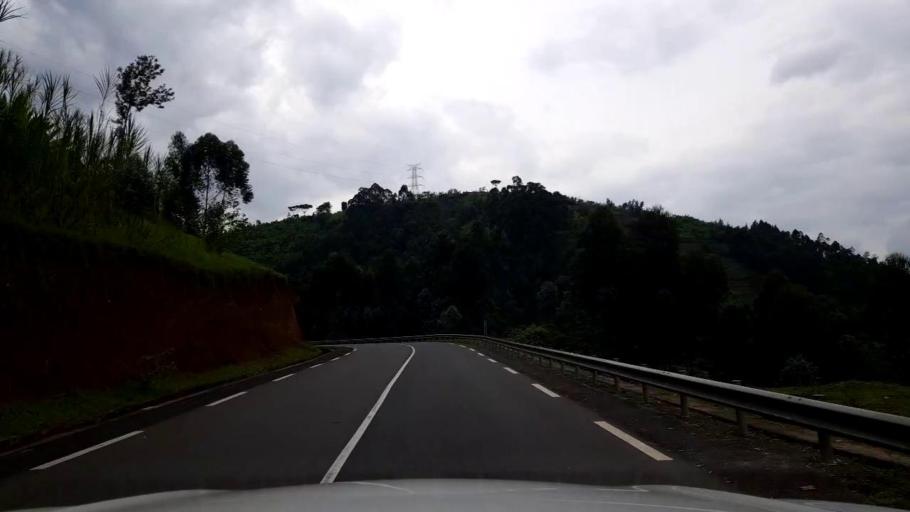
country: RW
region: Western Province
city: Kibuye
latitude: -1.9190
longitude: 29.3692
